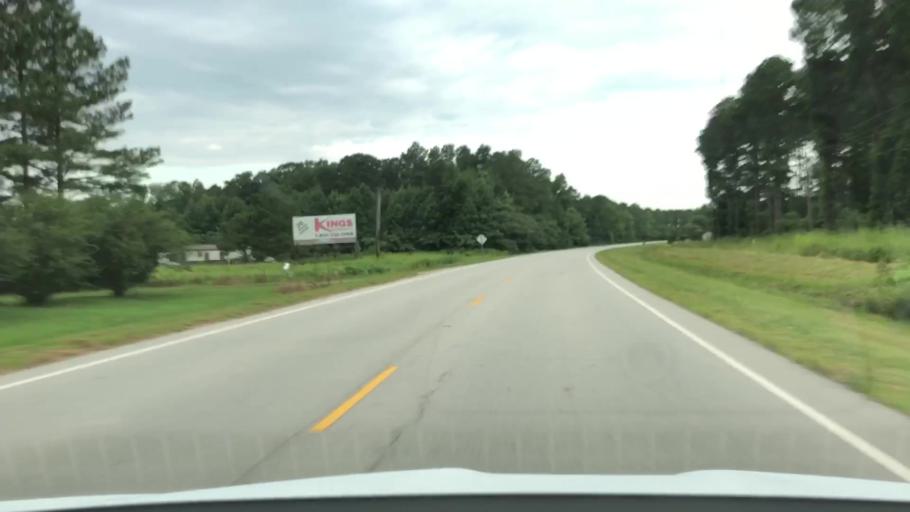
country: US
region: North Carolina
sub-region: Jones County
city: Trenton
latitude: 35.0360
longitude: -77.3408
